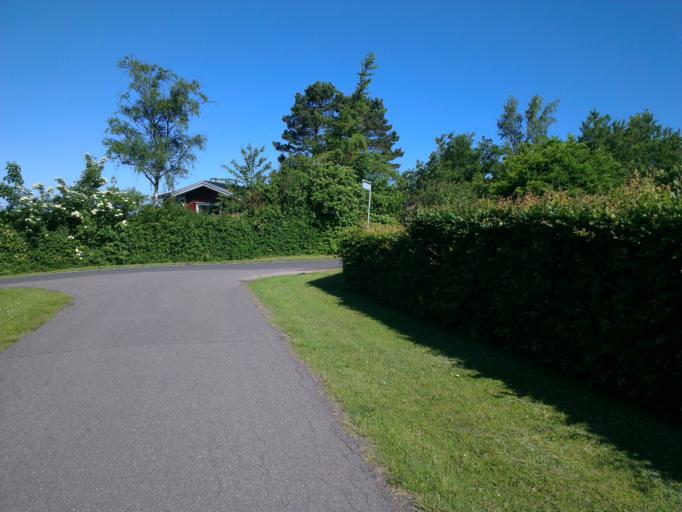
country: DK
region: Capital Region
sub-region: Halsnaes Kommune
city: Hundested
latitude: 55.9224
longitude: 11.9036
